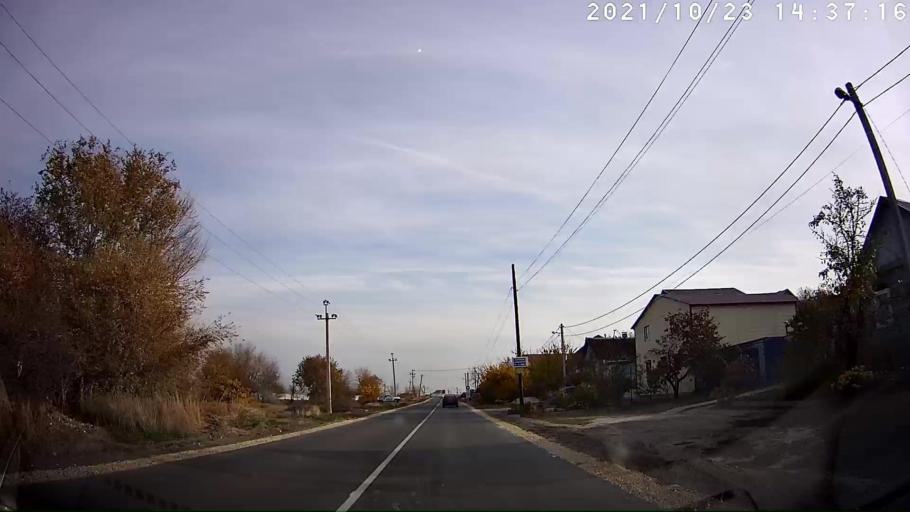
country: RU
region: Volgograd
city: Krasnoslobodsk
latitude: 48.4987
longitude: 44.5474
